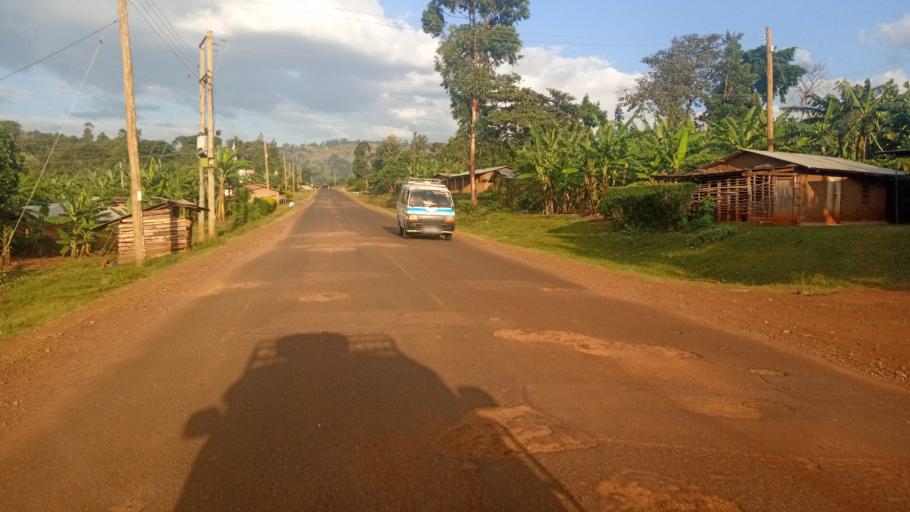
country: UG
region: Eastern Region
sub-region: Kapchorwa District
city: Kapchorwa
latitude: 1.3229
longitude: 34.3473
